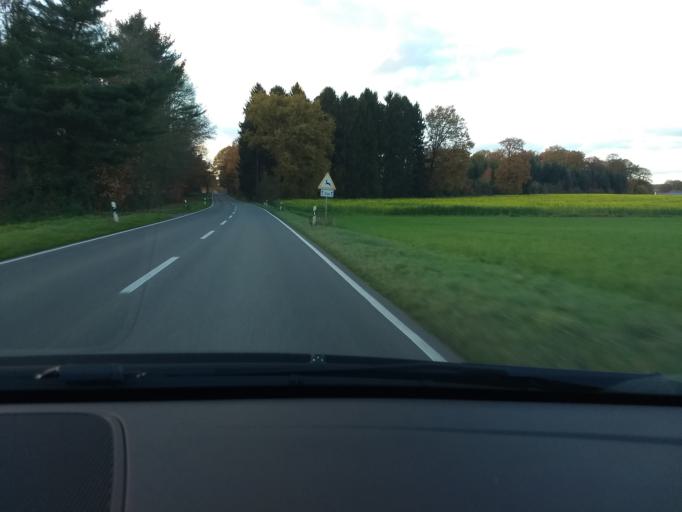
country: DE
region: North Rhine-Westphalia
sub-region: Regierungsbezirk Munster
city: Klein Reken
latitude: 51.7368
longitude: 7.0814
